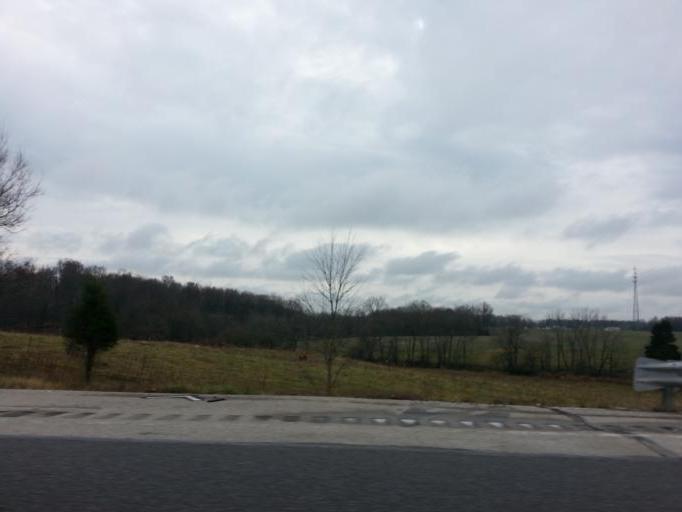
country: US
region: Indiana
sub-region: Ripley County
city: Sunman
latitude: 39.2805
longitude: -85.0943
